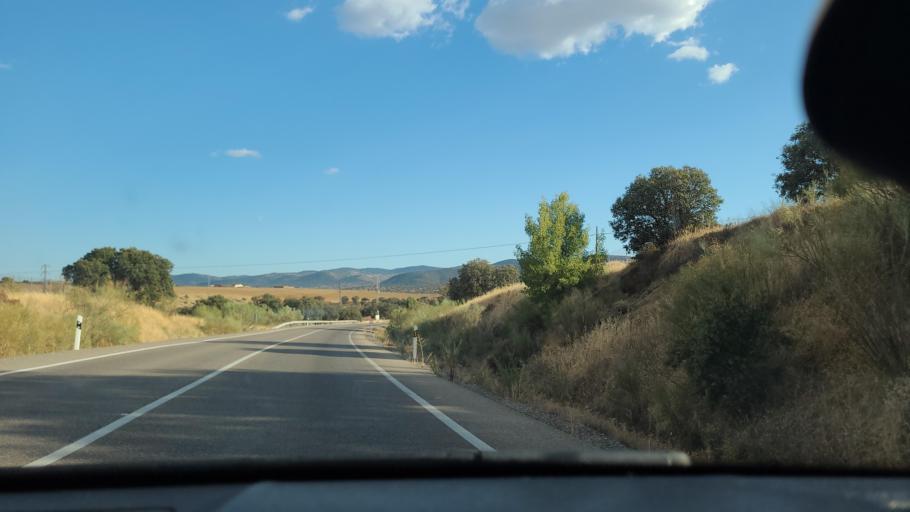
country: ES
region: Andalusia
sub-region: Province of Cordoba
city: Belmez
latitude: 38.2527
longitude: -5.1681
